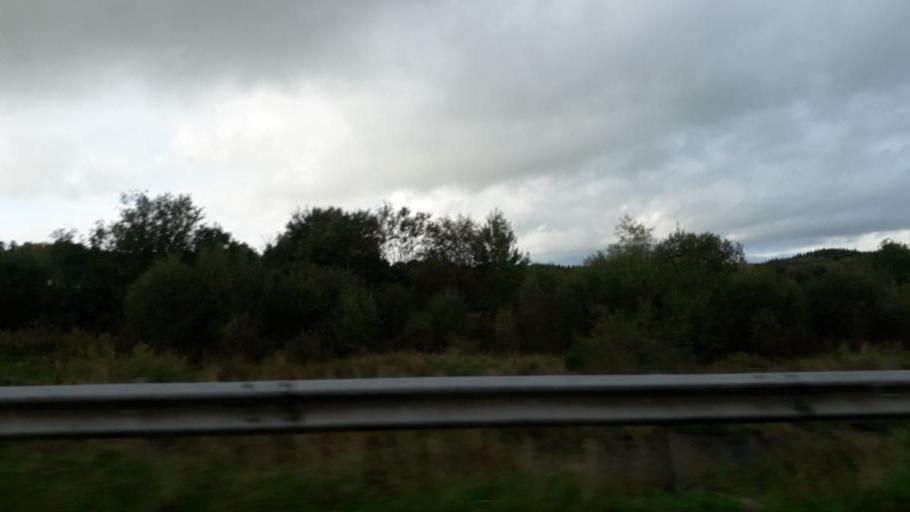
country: IE
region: Leinster
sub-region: An Longfort
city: Lanesborough
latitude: 53.7648
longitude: -8.0708
